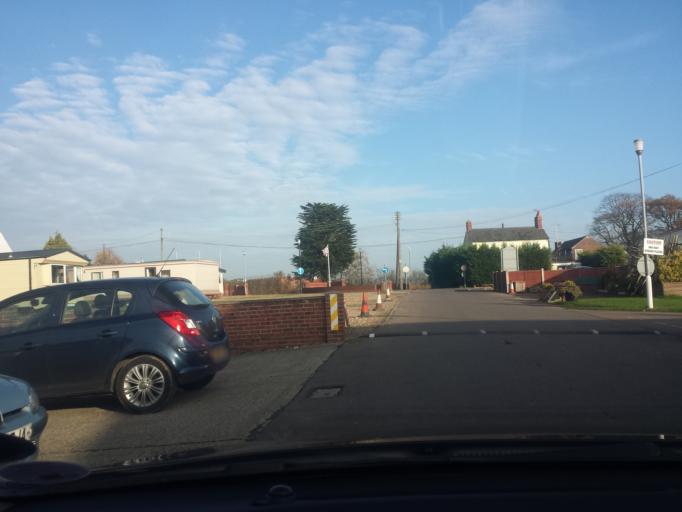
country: GB
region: England
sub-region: Essex
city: Saint Osyth
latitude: 51.8227
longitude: 1.0666
